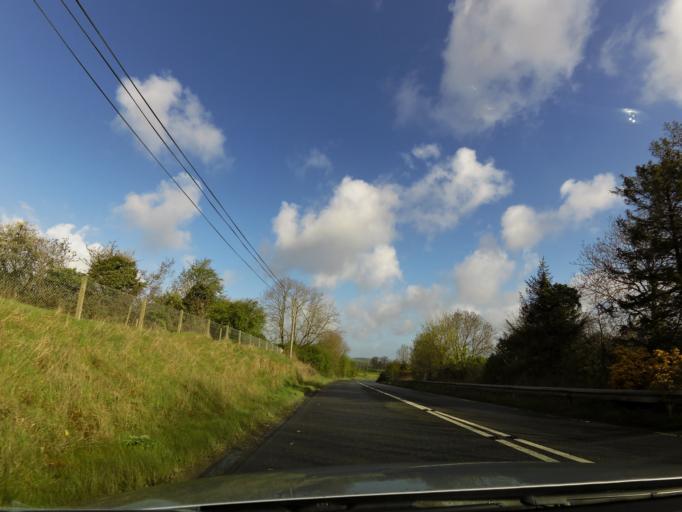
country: IE
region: Munster
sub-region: North Tipperary
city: Templemore
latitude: 52.7689
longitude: -8.0240
